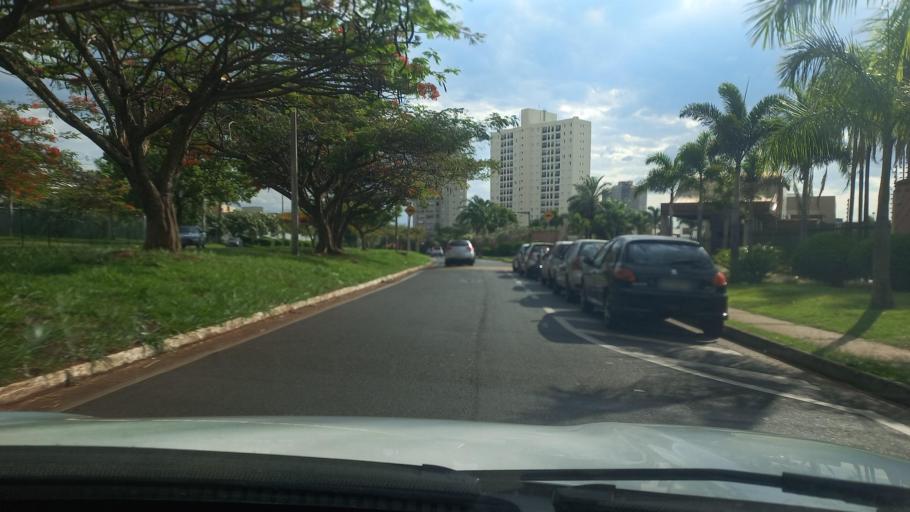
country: BR
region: Minas Gerais
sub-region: Uberaba
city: Uberaba
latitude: -19.7457
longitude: -47.9087
